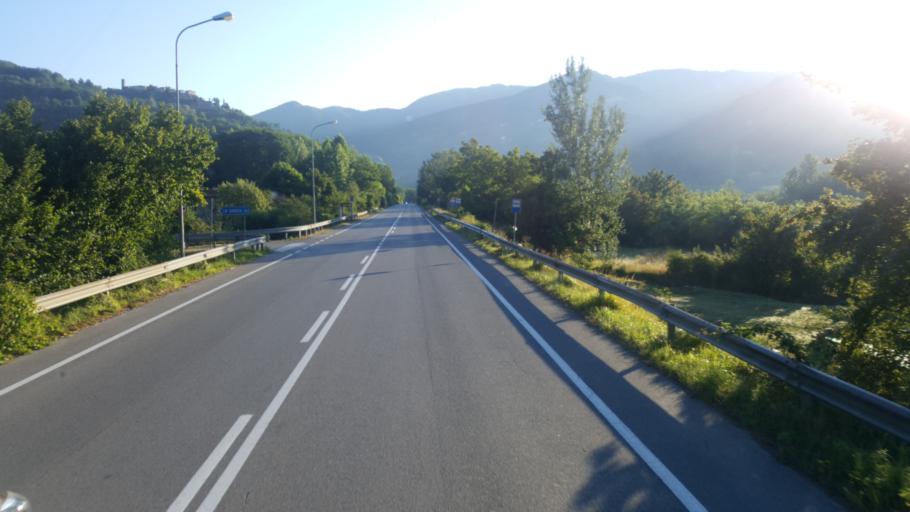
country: IT
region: Tuscany
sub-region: Provincia di Lucca
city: Gallicano
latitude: 44.0824
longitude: 10.4446
